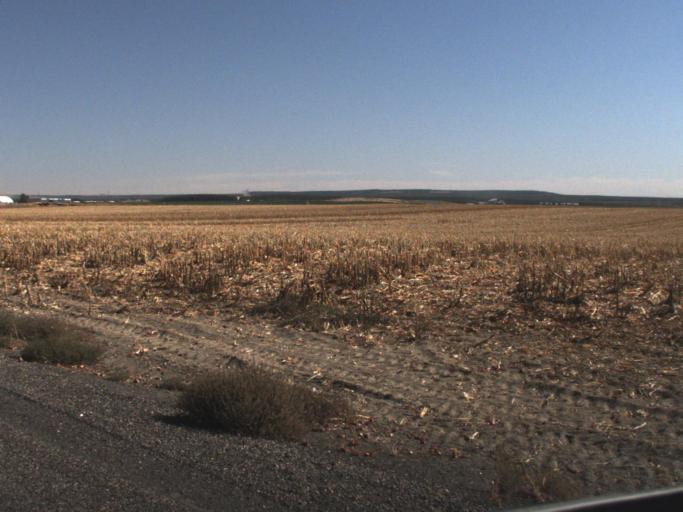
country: US
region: Washington
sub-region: Walla Walla County
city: Burbank
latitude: 46.2126
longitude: -118.9441
